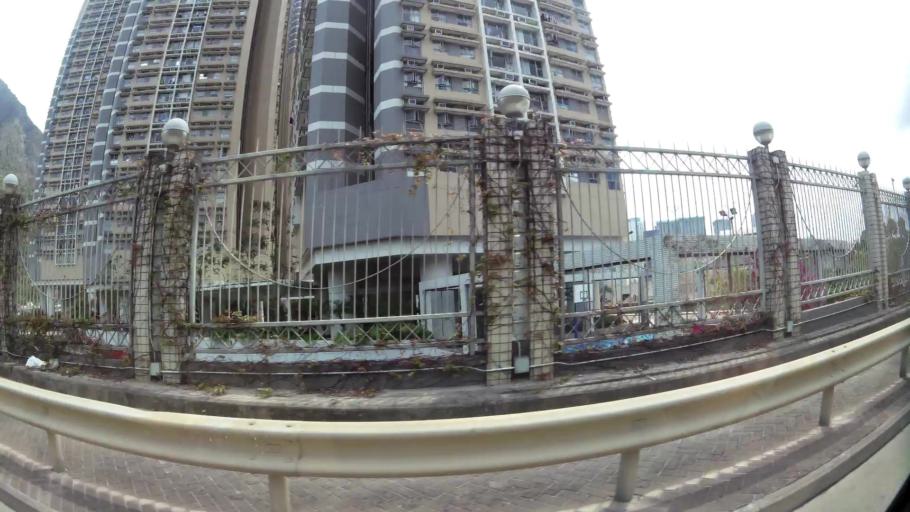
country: HK
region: Kowloon City
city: Kowloon
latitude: 22.3316
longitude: 114.2207
